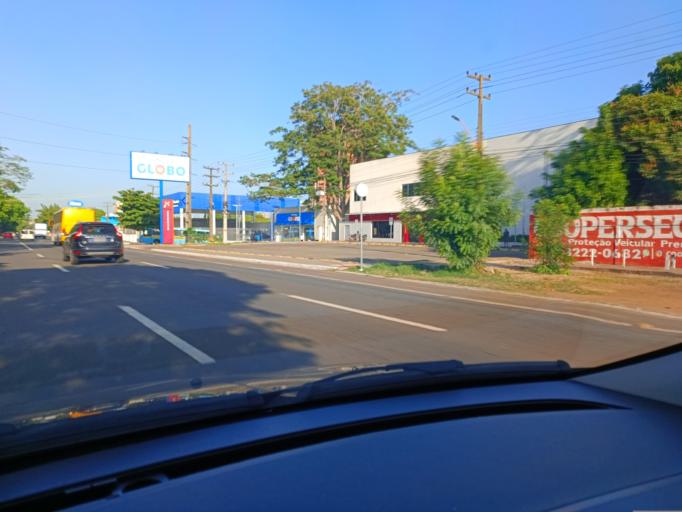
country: BR
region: Piaui
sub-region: Teresina
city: Teresina
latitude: -5.0816
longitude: -42.7699
